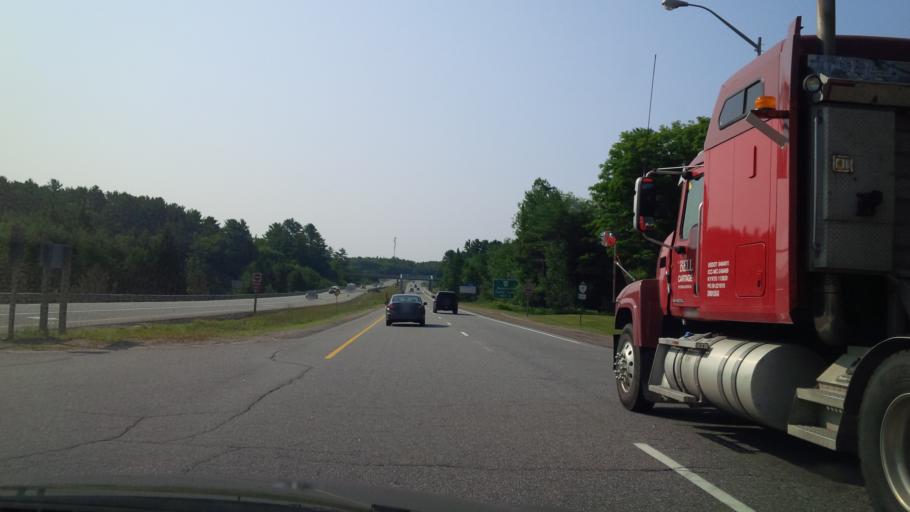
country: CA
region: Ontario
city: Bracebridge
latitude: 45.0910
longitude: -79.3017
